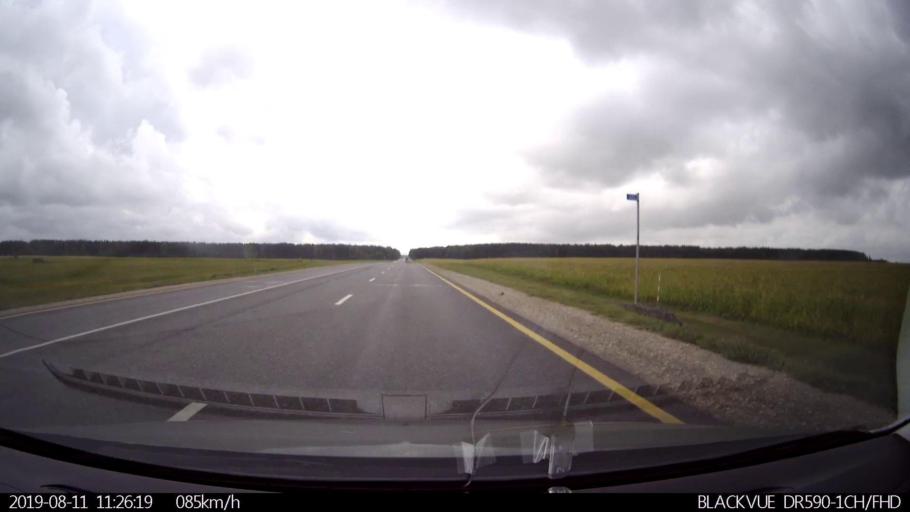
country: RU
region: Ulyanovsk
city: Krasnyy Gulyay
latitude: 54.1071
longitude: 48.2356
